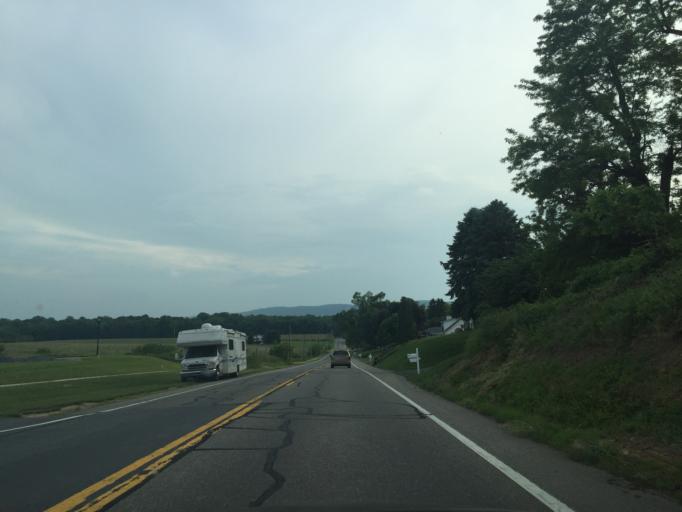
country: US
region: Maryland
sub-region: Frederick County
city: Brunswick
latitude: 39.3347
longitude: -77.6436
